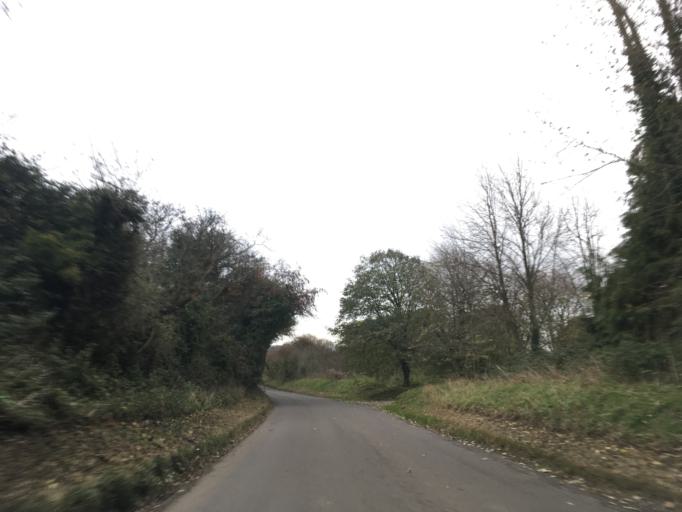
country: GB
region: England
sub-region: South Gloucestershire
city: Hinton
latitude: 51.4889
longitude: -2.3938
